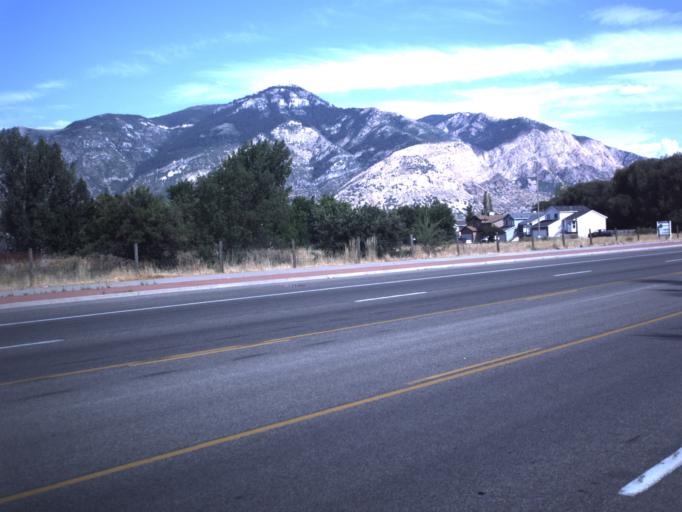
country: US
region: Utah
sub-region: Weber County
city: Harrisville
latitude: 41.2956
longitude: -111.9955
